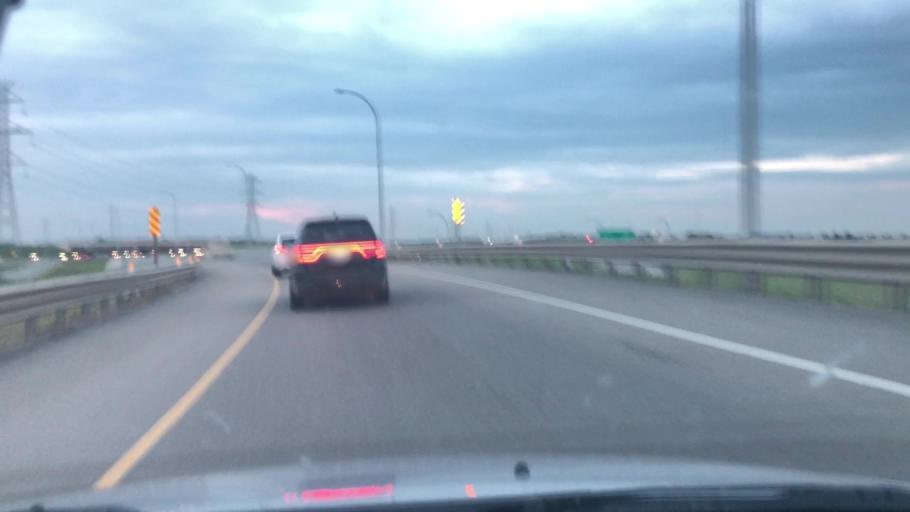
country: CA
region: Alberta
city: St. Albert
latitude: 53.5178
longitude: -113.6568
